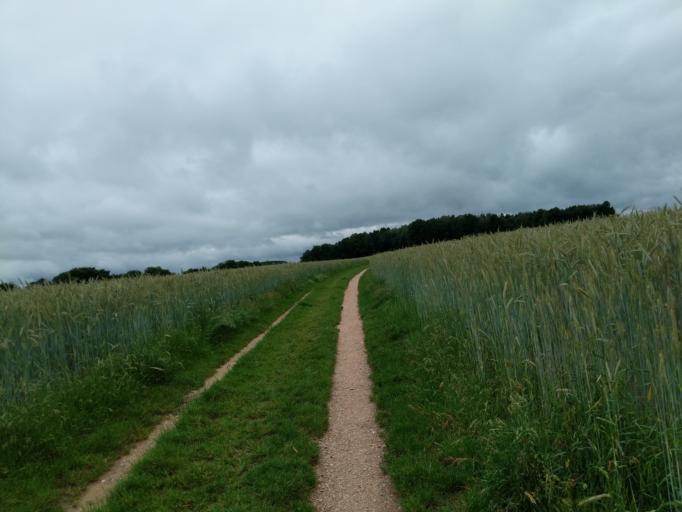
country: DE
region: Bavaria
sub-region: Upper Palatinate
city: Lappersdorf
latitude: 49.0647
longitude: 12.0817
